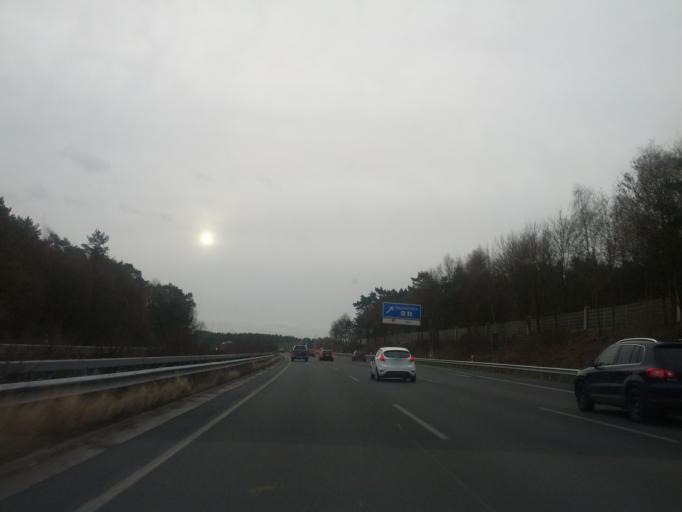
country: DE
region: Lower Saxony
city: Marxen
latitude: 53.3359
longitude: 10.0404
